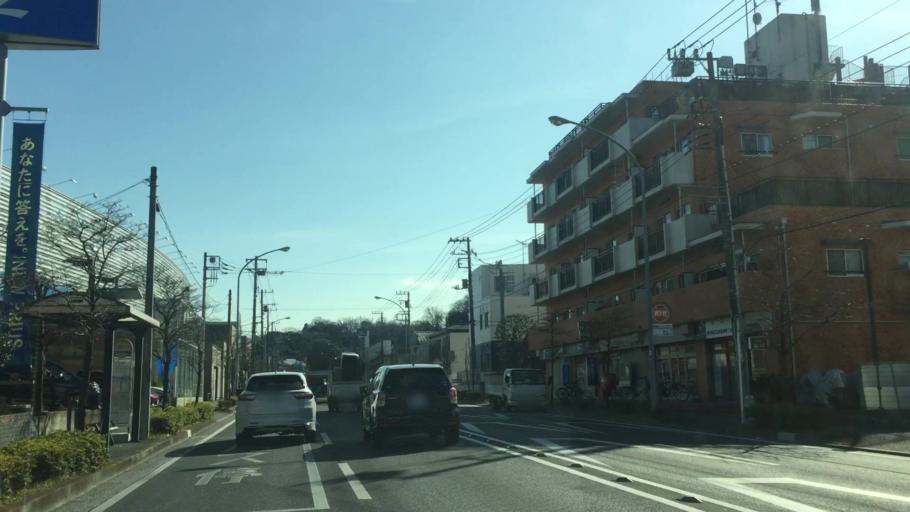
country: JP
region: Kanagawa
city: Yokohama
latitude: 35.3712
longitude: 139.6122
